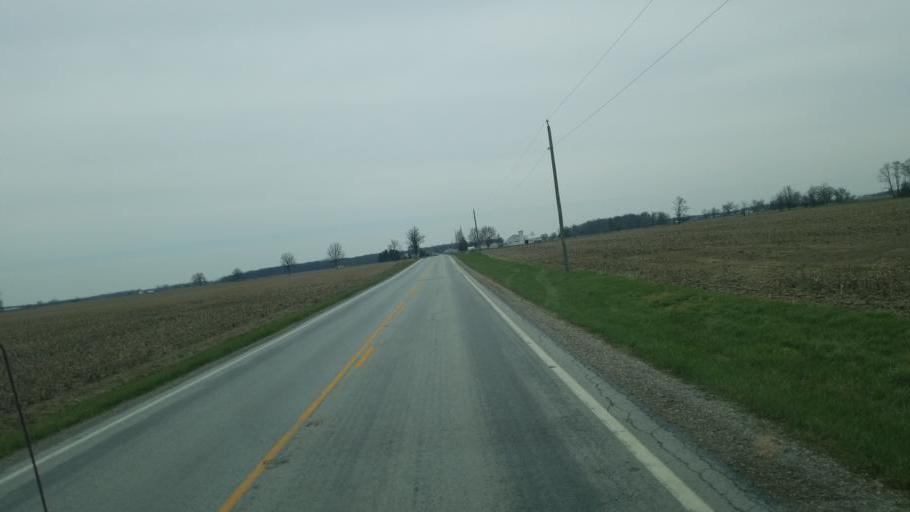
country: US
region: Ohio
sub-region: Hardin County
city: Forest
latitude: 40.8775
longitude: -83.5246
